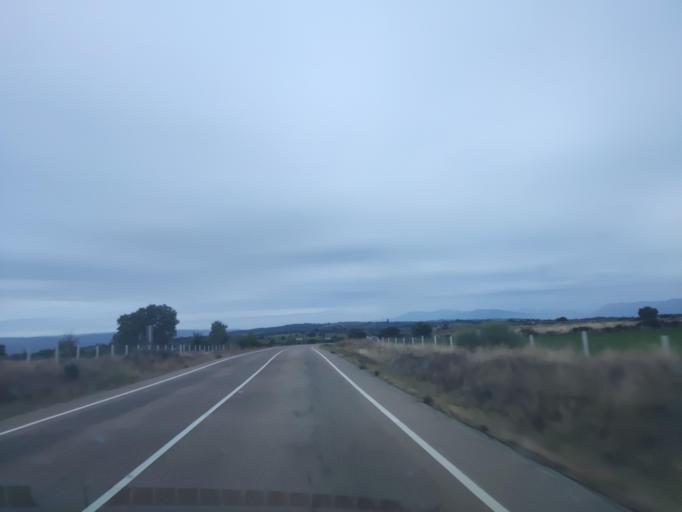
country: ES
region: Castille and Leon
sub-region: Provincia de Salamanca
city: Hinojosa de Duero
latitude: 40.9674
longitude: -6.8133
